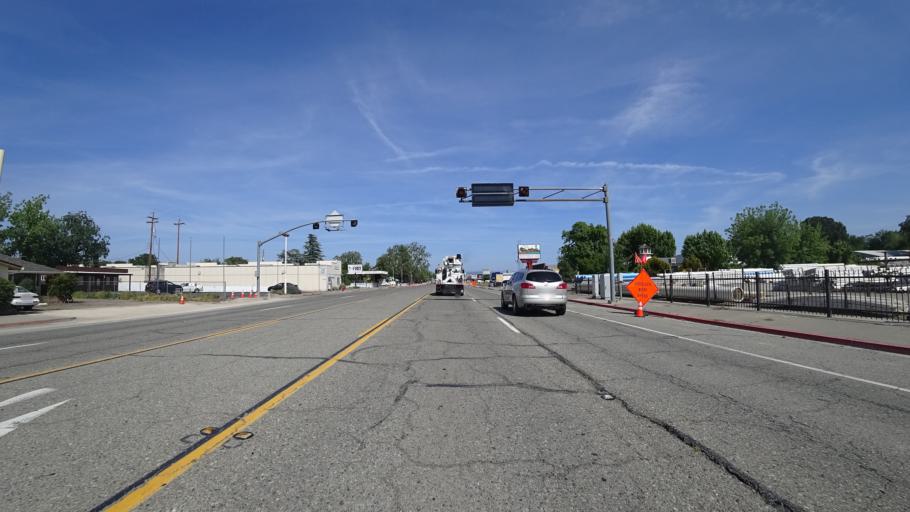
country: US
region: California
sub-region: Tehama County
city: Red Bluff
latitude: 40.1860
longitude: -122.2066
